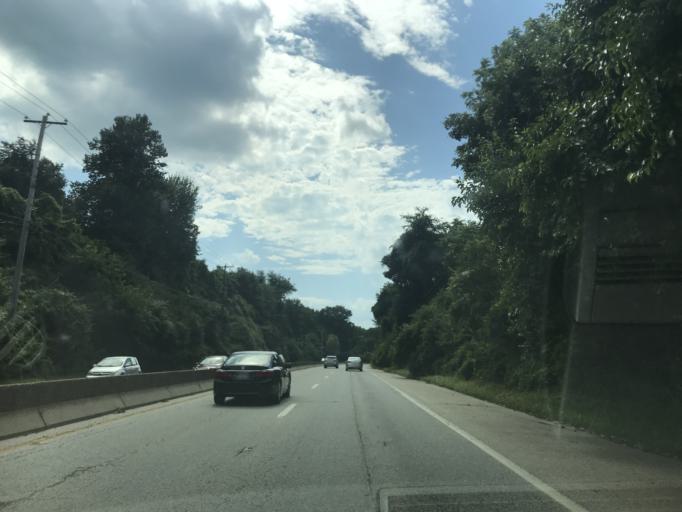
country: US
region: Pennsylvania
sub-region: Chester County
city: West Chester
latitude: 39.8716
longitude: -75.6018
